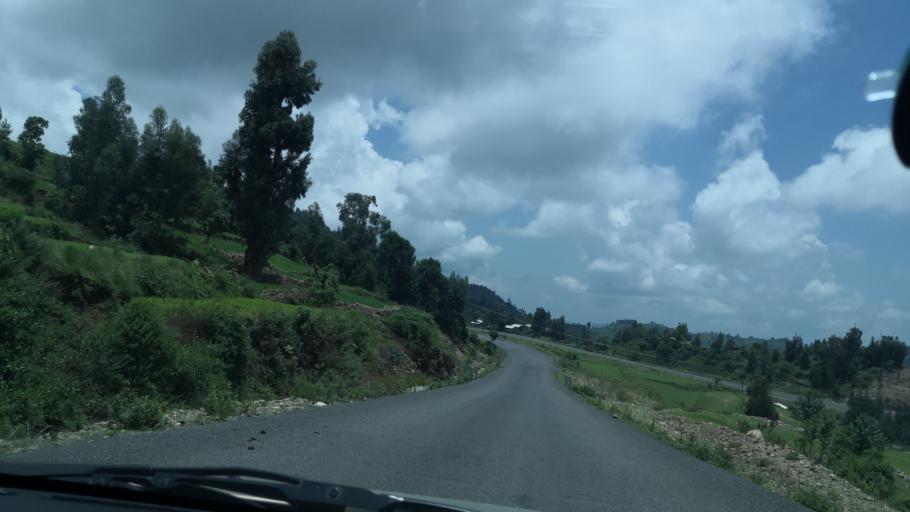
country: ET
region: Amhara
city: Abomsa
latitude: 10.3305
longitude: 39.8461
